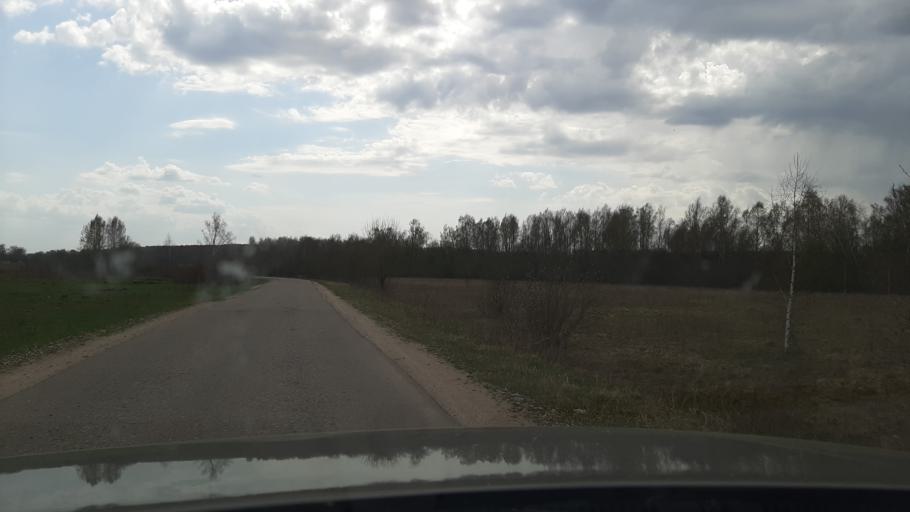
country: RU
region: Ivanovo
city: Furmanov
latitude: 57.3102
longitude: 41.1626
